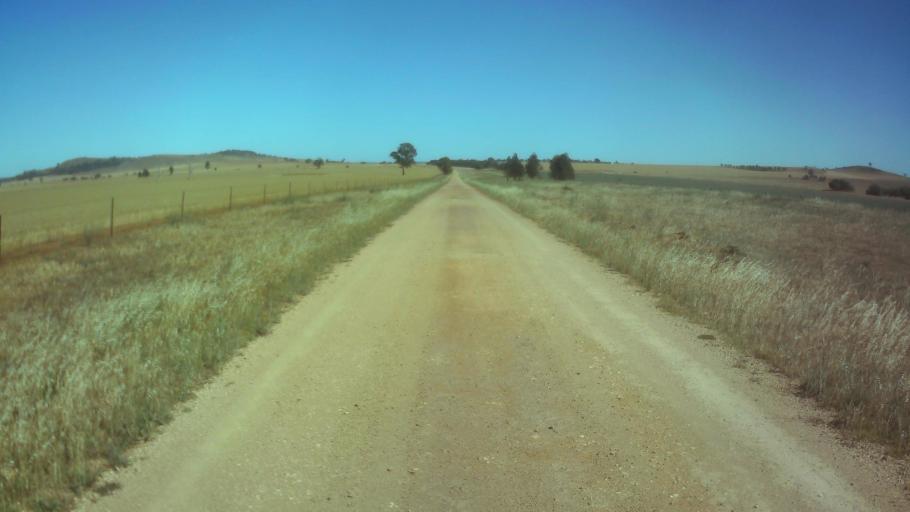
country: AU
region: New South Wales
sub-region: Weddin
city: Grenfell
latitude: -33.9768
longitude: 148.3241
